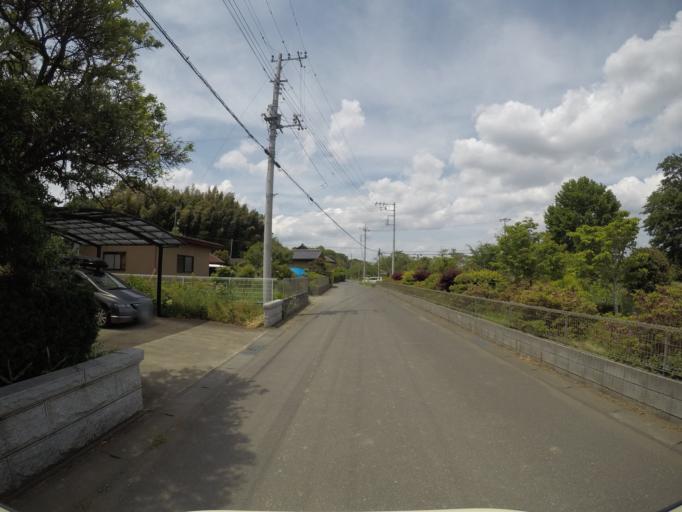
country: JP
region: Ibaraki
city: Ushiku
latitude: 35.9597
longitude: 140.1237
